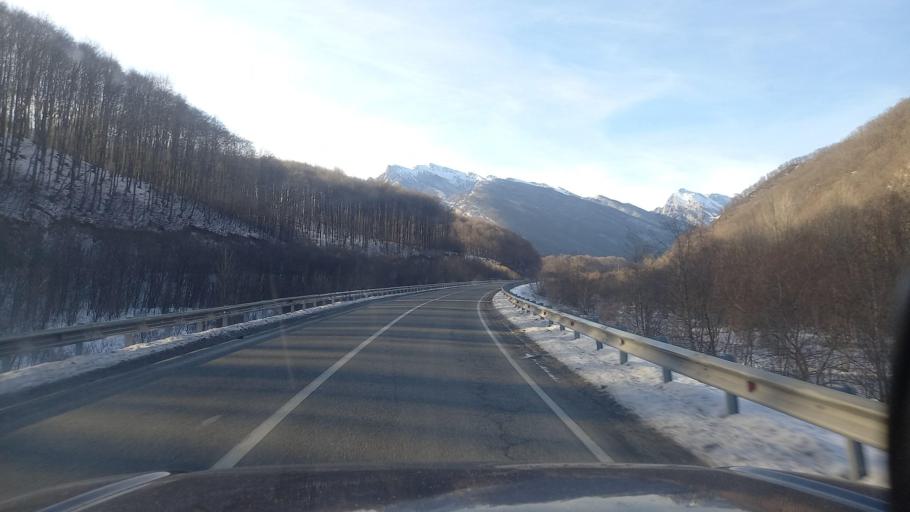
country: RU
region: North Ossetia
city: Gizel'
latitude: 42.9369
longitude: 44.5567
